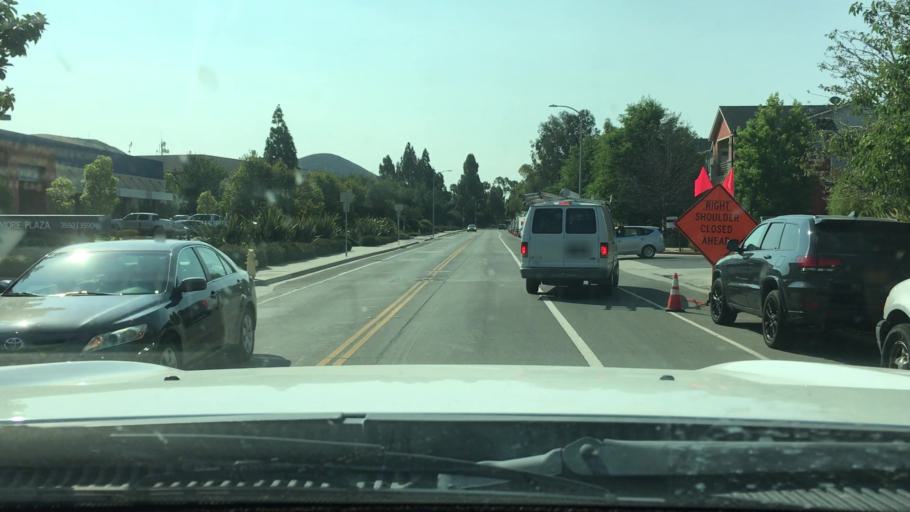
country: US
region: California
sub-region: San Luis Obispo County
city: San Luis Obispo
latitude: 35.2560
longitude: -120.6430
